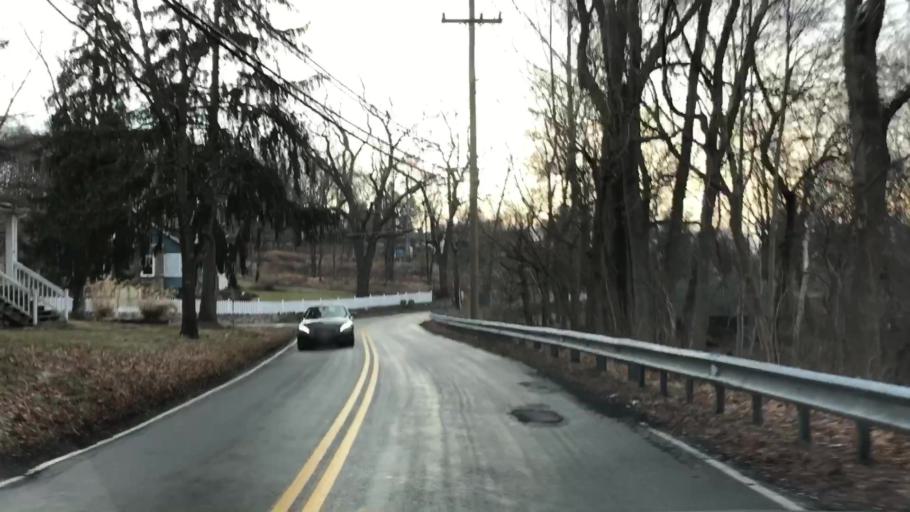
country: US
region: New York
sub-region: Rockland County
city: Stony Point
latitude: 41.2319
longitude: -73.9947
